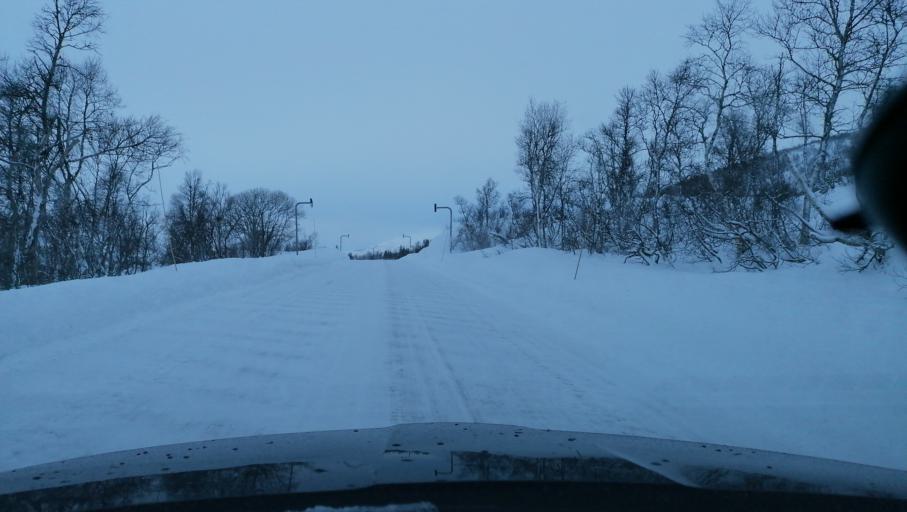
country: NO
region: Aust-Agder
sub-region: Bykle
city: Hovden
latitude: 59.6355
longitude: 7.4538
